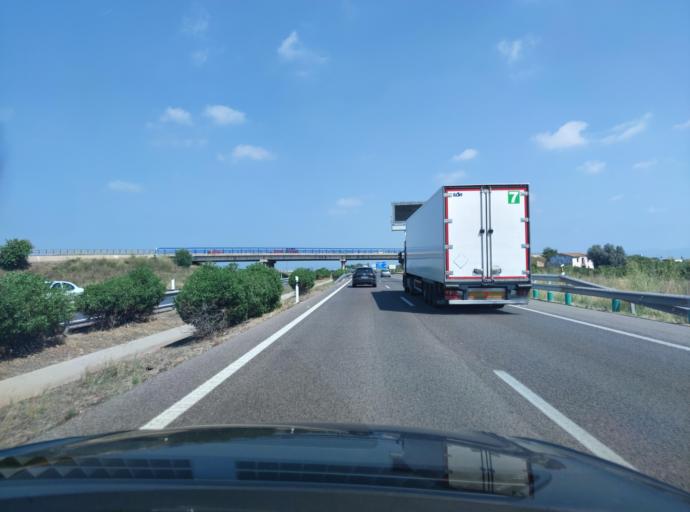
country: ES
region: Valencia
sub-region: Provincia de Castello
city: Alquerias del Nino Perdido
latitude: 39.8863
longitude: -0.1267
